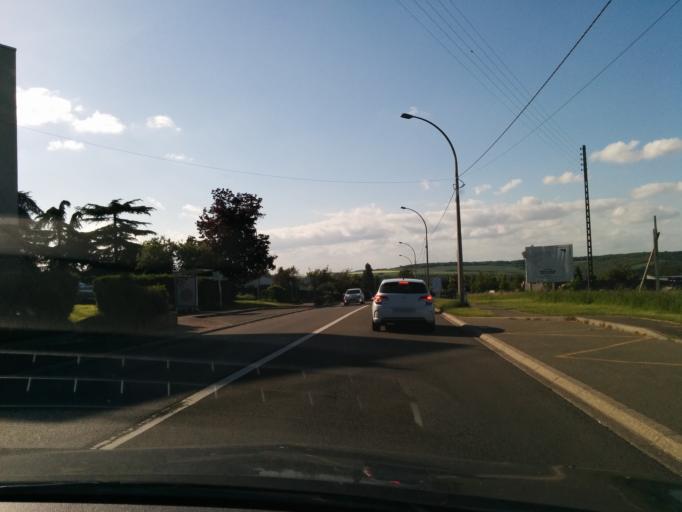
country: FR
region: Ile-de-France
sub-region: Departement des Yvelines
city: Freneuse
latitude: 49.0336
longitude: 1.6017
